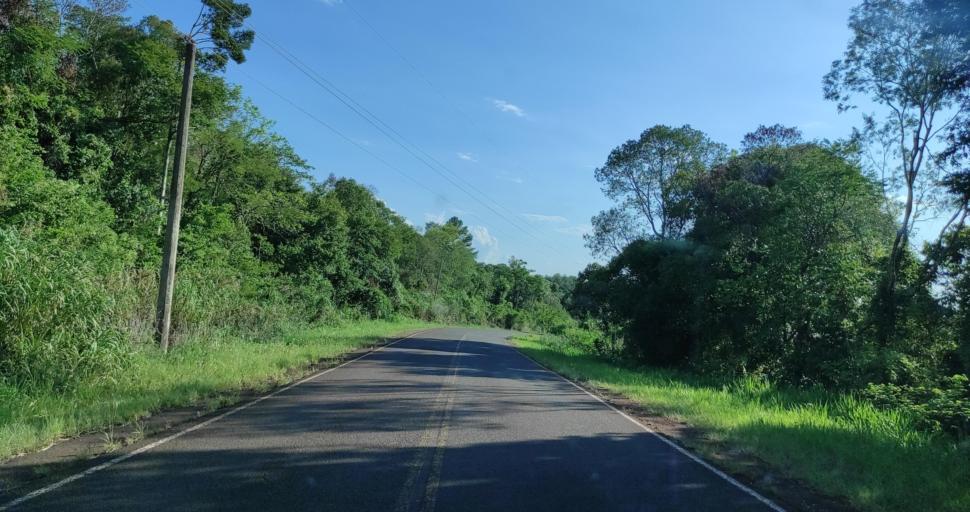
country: AR
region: Misiones
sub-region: Departamento de Eldorado
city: Eldorado
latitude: -26.3783
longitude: -54.3374
